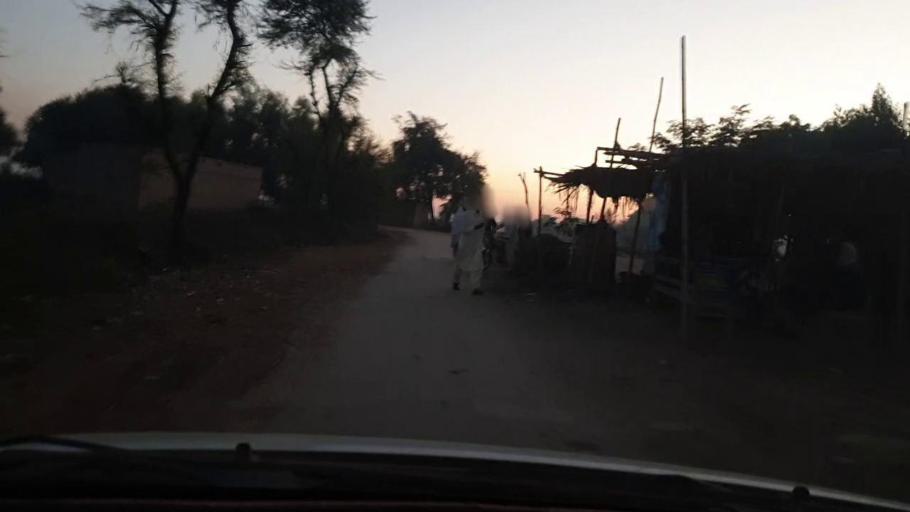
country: PK
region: Sindh
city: Khairpur Nathan Shah
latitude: 27.1382
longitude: 67.7176
